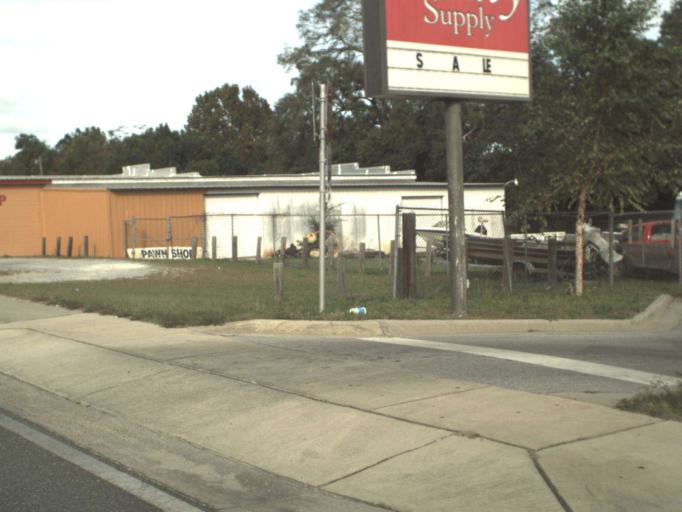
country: US
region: Florida
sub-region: Escambia County
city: Goulding
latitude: 30.4398
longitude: -87.2401
